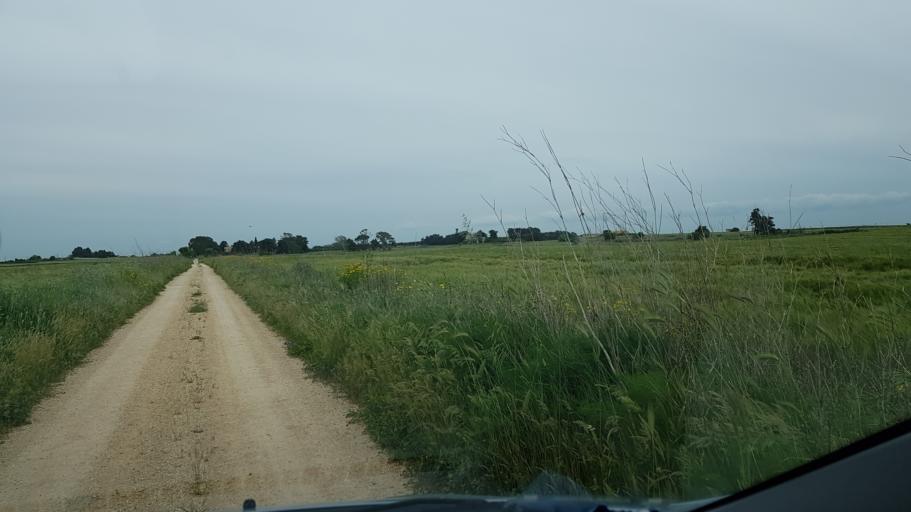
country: IT
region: Apulia
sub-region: Provincia di Brindisi
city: Brindisi
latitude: 40.6544
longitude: 17.8819
